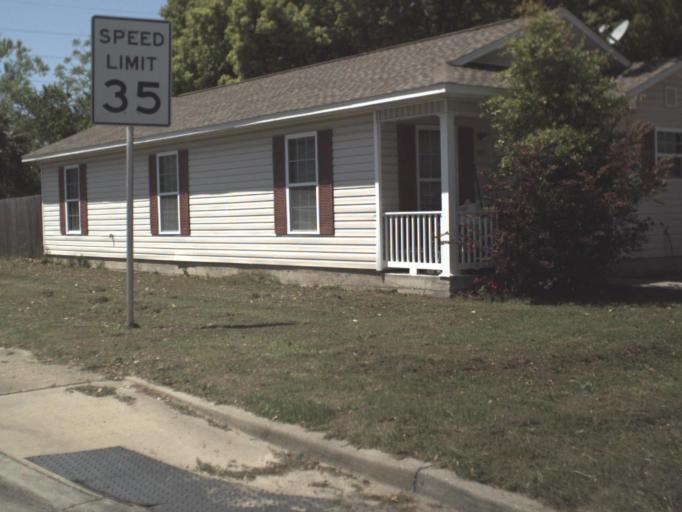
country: US
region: Florida
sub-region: Escambia County
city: Pensacola
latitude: 30.4201
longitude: -87.2267
